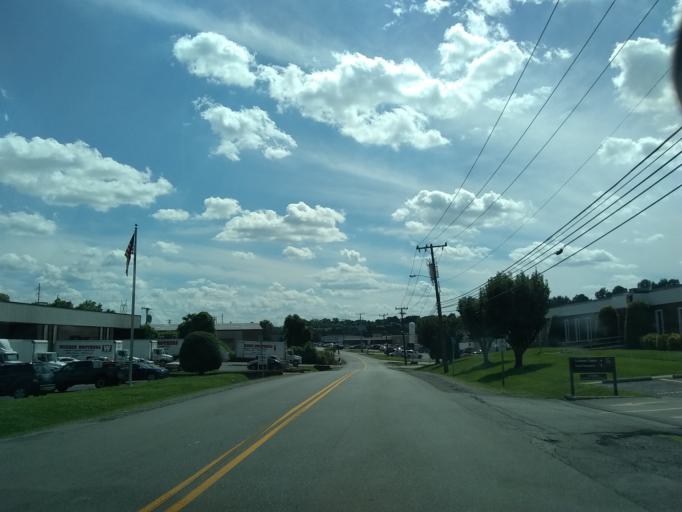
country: US
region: Tennessee
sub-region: Davidson County
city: Nashville
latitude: 36.1520
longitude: -86.7065
